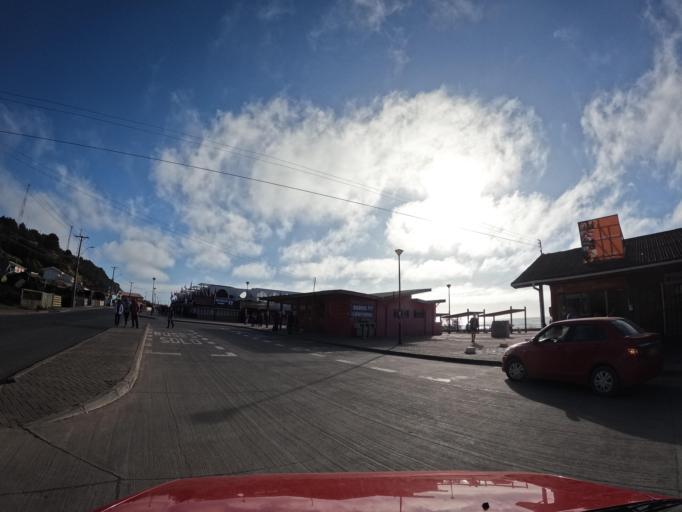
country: CL
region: Maule
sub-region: Provincia de Talca
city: Constitucion
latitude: -34.9374
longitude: -72.1821
